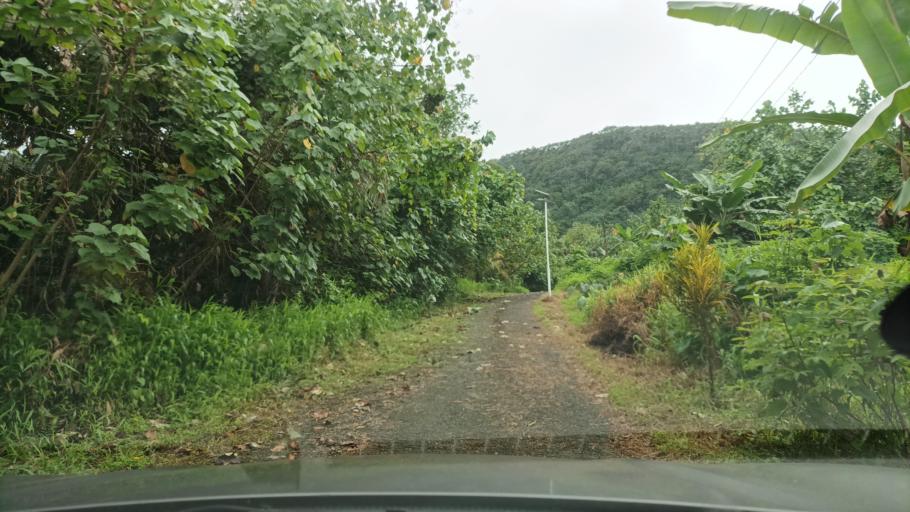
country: FM
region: Pohnpei
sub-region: Kolonia Municipality
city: Kolonia
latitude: 6.9405
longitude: 158.2670
